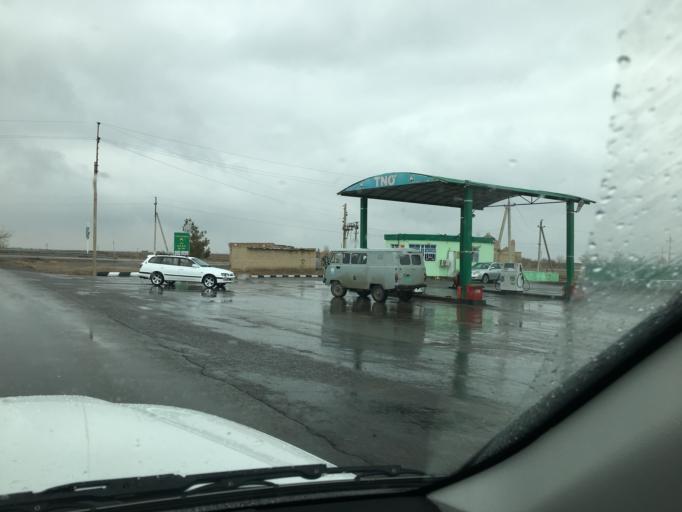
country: TM
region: Mary
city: Bayramaly
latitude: 37.4088
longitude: 62.1697
